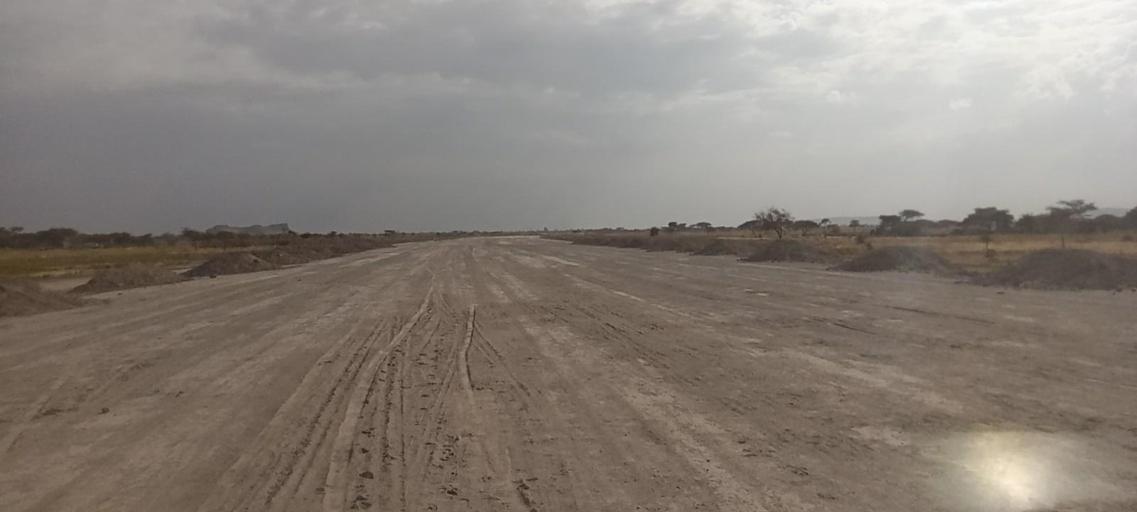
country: ET
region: Oromiya
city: Ziway
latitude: 7.8739
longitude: 38.6726
